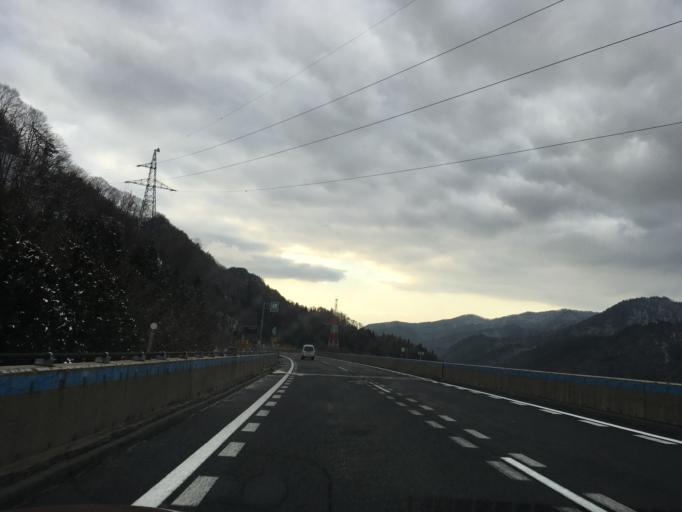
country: JP
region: Yamagata
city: Yamagata-shi
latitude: 38.2245
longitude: 140.4239
